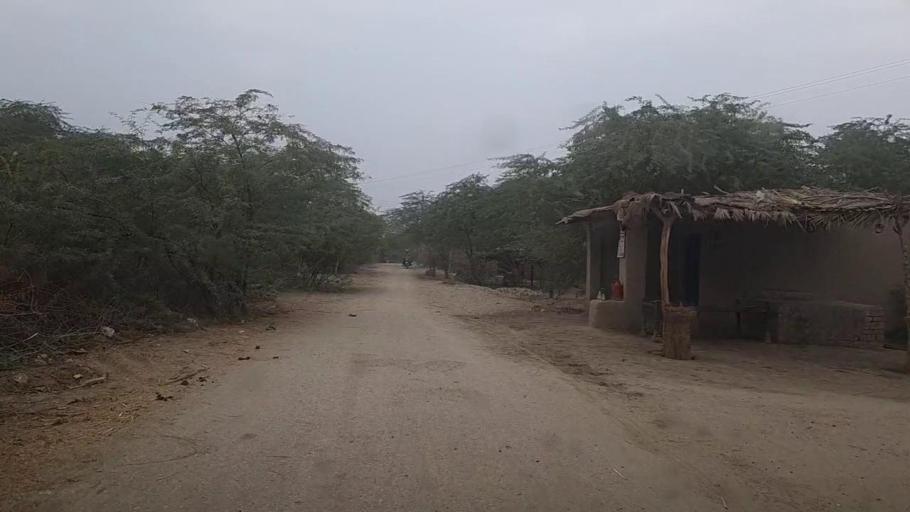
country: PK
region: Sindh
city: Gambat
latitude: 27.3490
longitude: 68.6014
